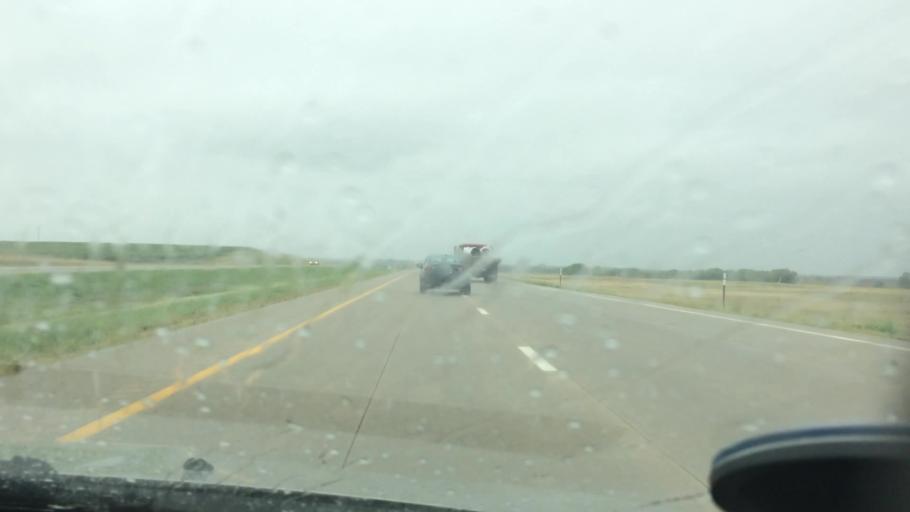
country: US
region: Kansas
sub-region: Ellsworth County
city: Ellsworth
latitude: 38.8494
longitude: -98.2856
